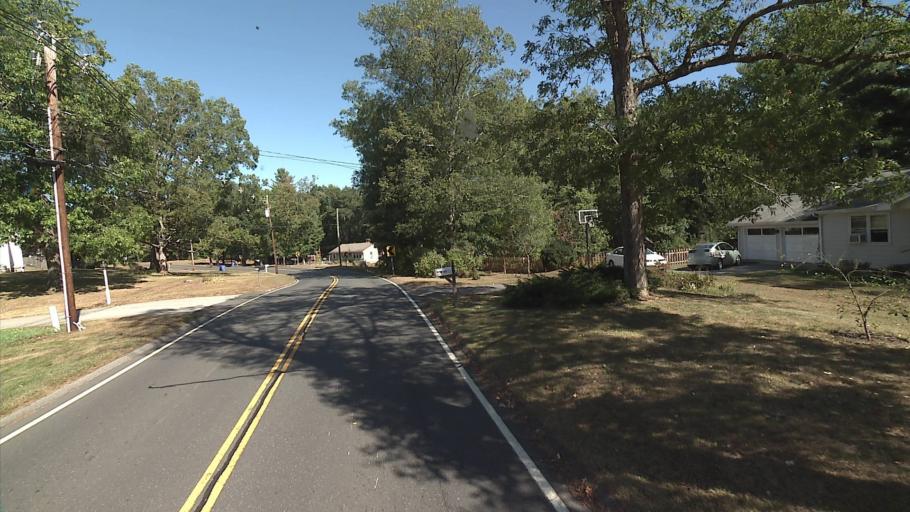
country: US
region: Connecticut
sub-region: Hartford County
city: Glastonbury Center
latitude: 41.6972
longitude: -72.5310
